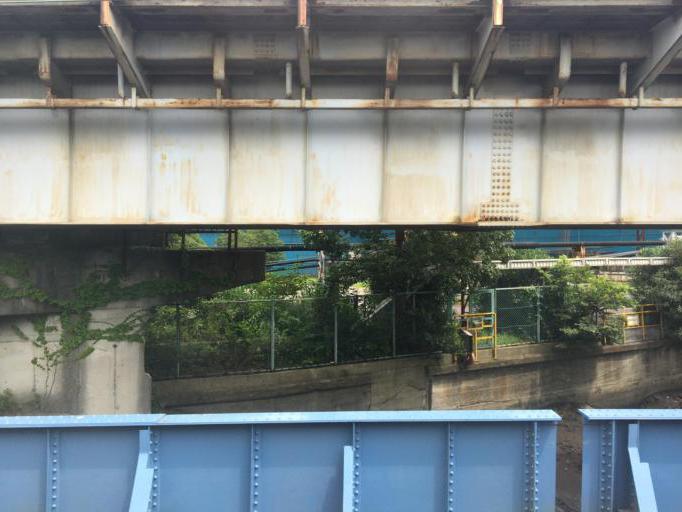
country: JP
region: Kanagawa
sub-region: Kawasaki-shi
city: Kawasaki
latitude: 35.5079
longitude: 139.7104
